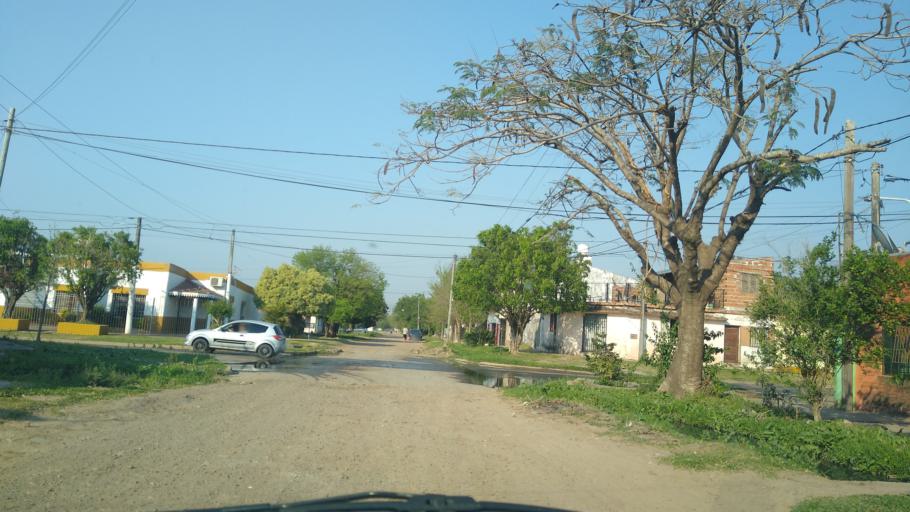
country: AR
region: Chaco
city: Barranqueras
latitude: -27.4787
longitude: -58.9297
